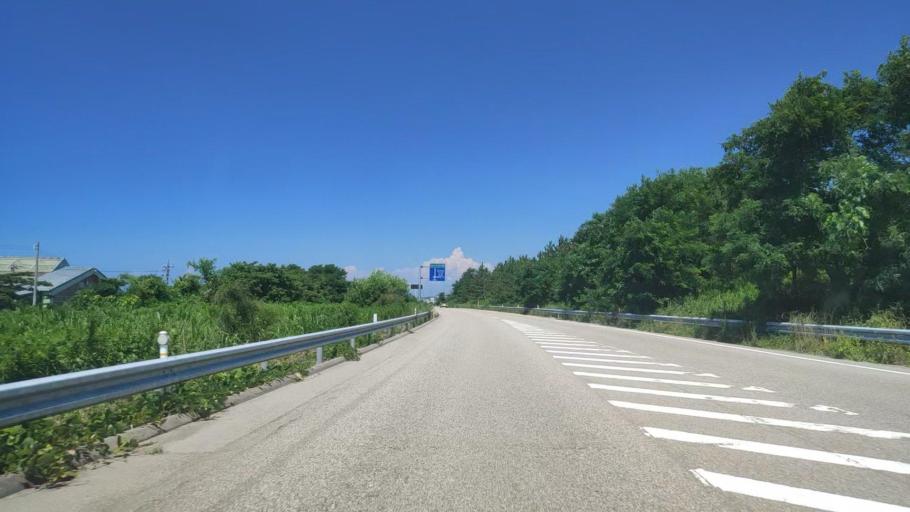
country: JP
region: Ishikawa
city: Kanazawa-shi
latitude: 36.6334
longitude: 136.6179
